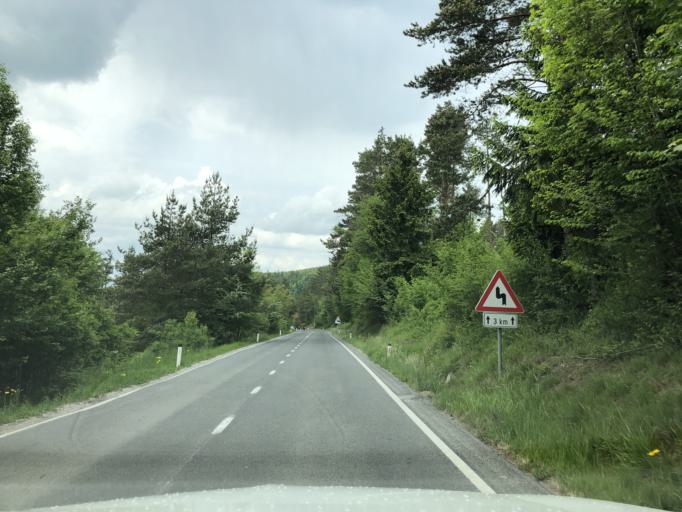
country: SI
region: Bloke
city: Nova Vas
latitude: 45.7616
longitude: 14.4597
